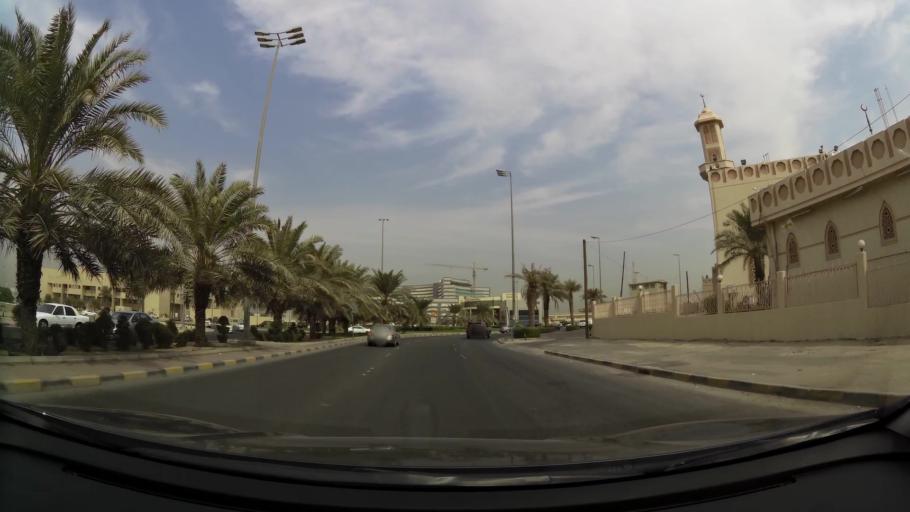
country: KW
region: Al Farwaniyah
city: Janub as Surrah
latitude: 29.2705
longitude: 48.0161
